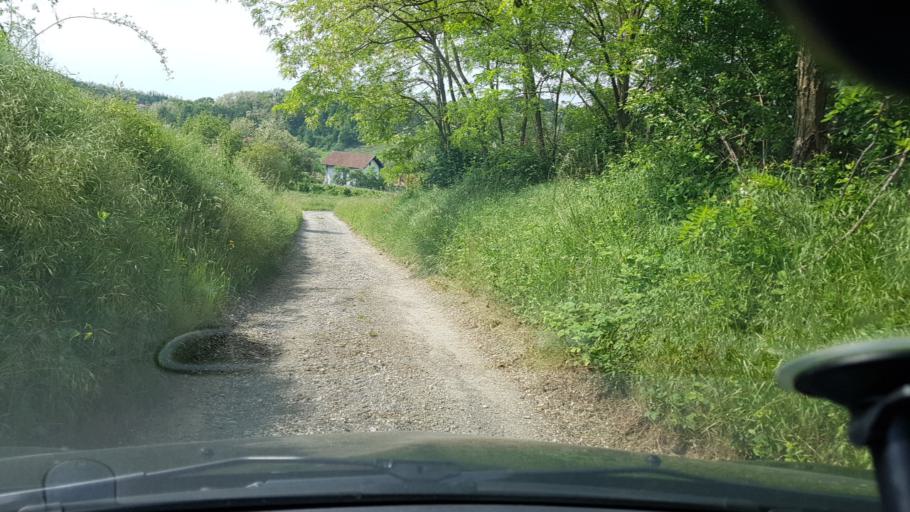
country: HR
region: Krapinsko-Zagorska
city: Marija Bistrica
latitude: 45.9367
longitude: 16.2096
